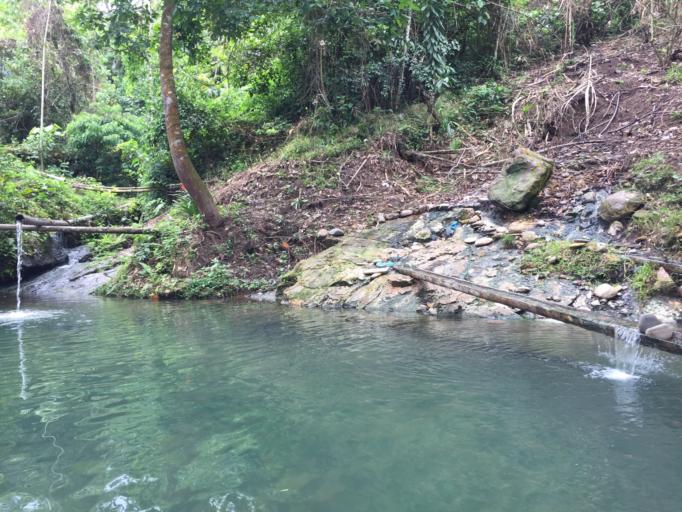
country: PE
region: Cusco
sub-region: Provincia de Paucartambo
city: Pillcopata
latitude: -12.6686
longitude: -71.2691
